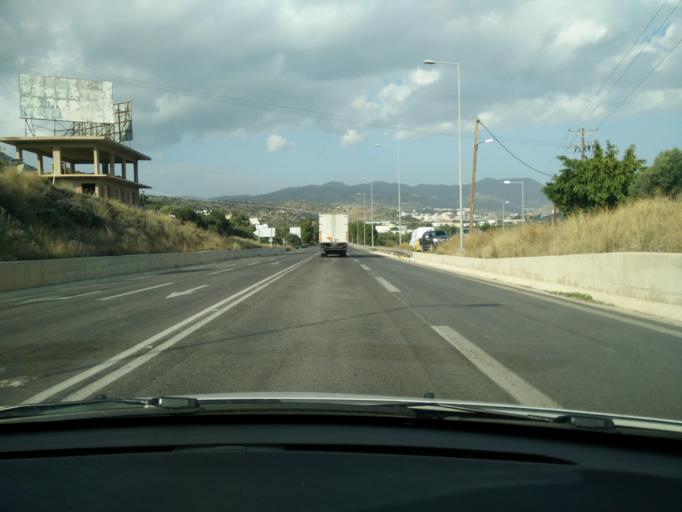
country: GR
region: Crete
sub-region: Nomos Lasithiou
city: Agios Nikolaos
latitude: 35.1874
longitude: 25.7041
